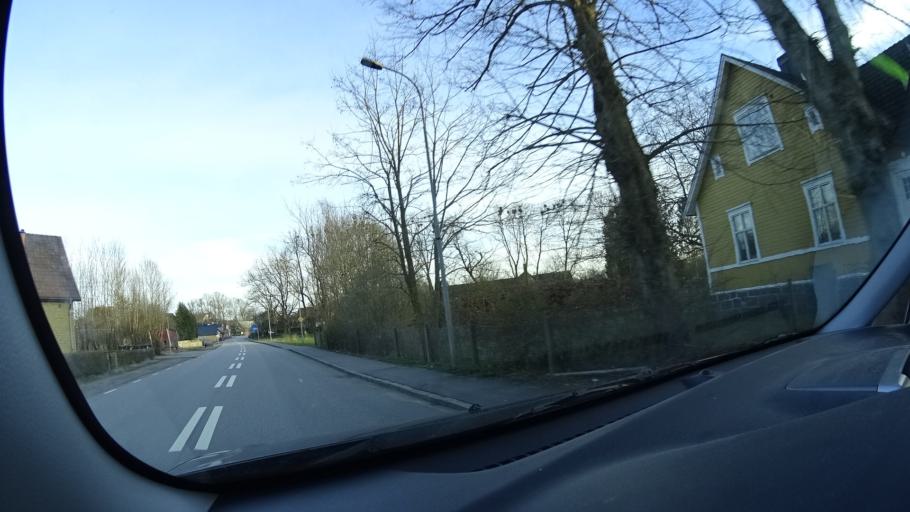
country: SE
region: Skane
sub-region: Eslovs Kommun
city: Stehag
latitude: 55.9639
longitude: 13.3313
